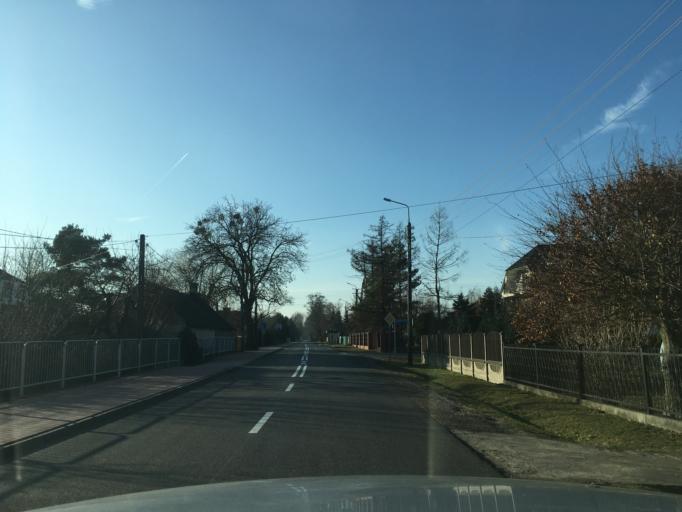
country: PL
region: Lodz Voivodeship
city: Zabia Wola
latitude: 52.0485
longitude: 20.7553
